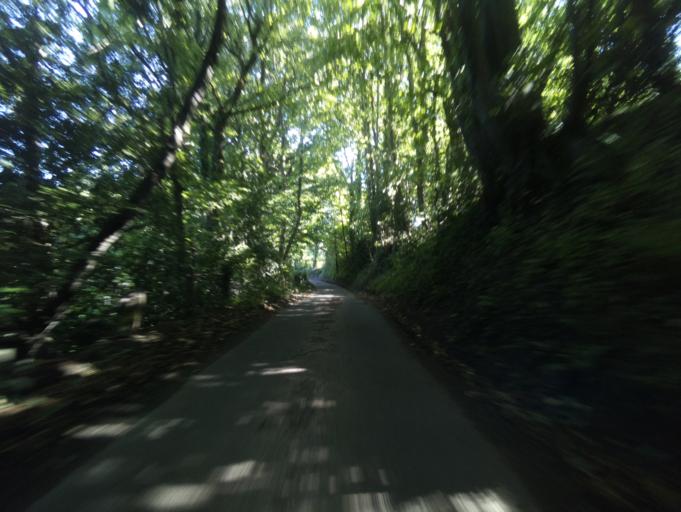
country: GB
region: Wales
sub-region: Torfaen County Borough
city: Cwmbran
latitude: 51.6217
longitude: -3.0357
